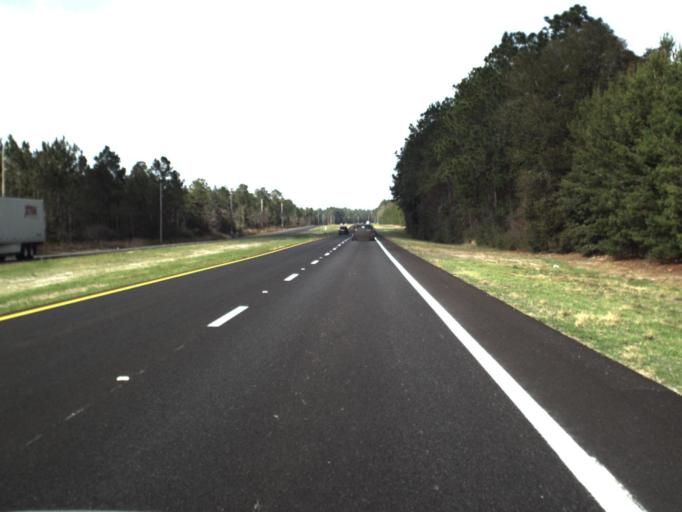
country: US
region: Florida
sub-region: Bay County
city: Youngstown
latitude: 30.3886
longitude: -85.4364
